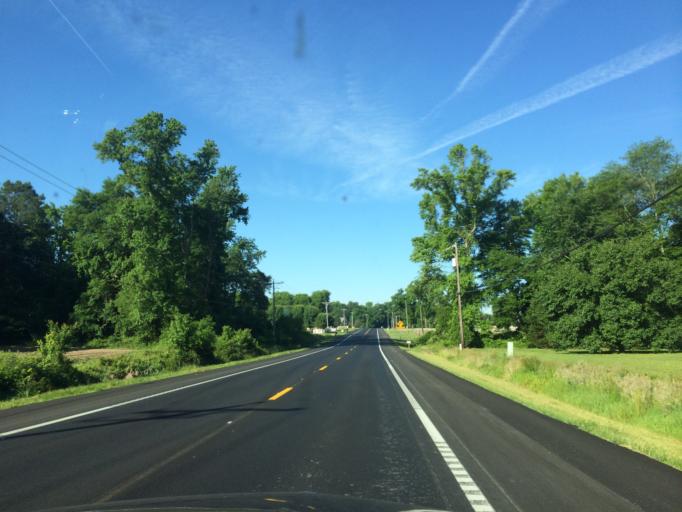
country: US
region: Maryland
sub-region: Wicomico County
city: Hebron
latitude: 38.3589
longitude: -75.7002
